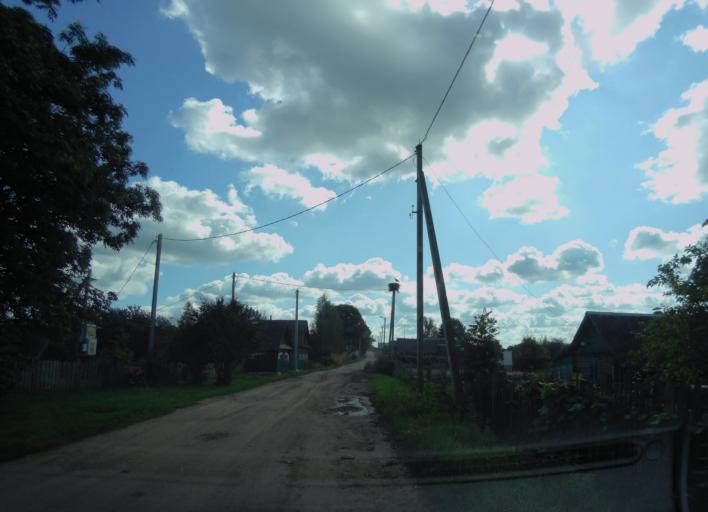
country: BY
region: Minsk
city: Zyembin
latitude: 54.3763
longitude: 28.3762
